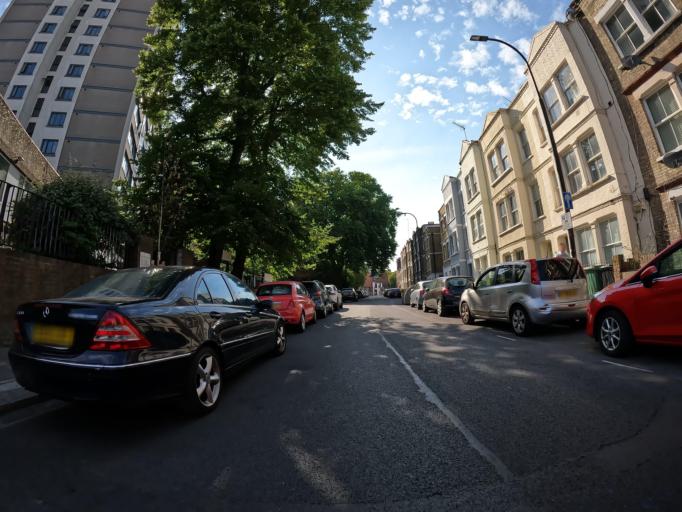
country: GB
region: England
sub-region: Greater London
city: Hendon
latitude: 51.5904
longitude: -0.2221
